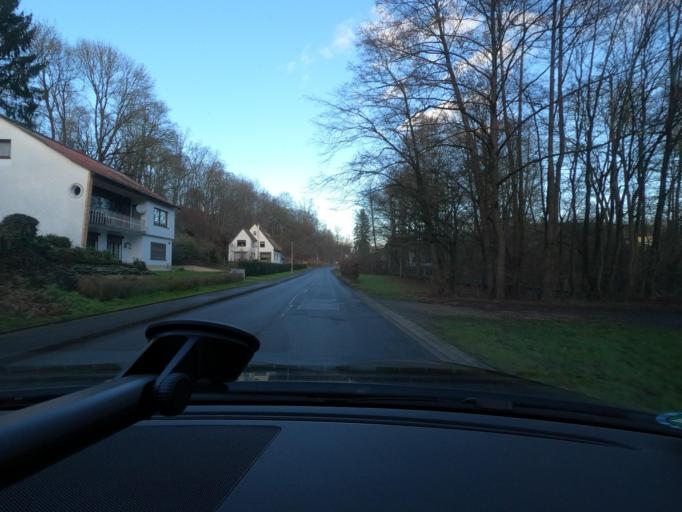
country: DE
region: Lower Saxony
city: Rhumspringe
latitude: 51.5888
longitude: 10.3049
